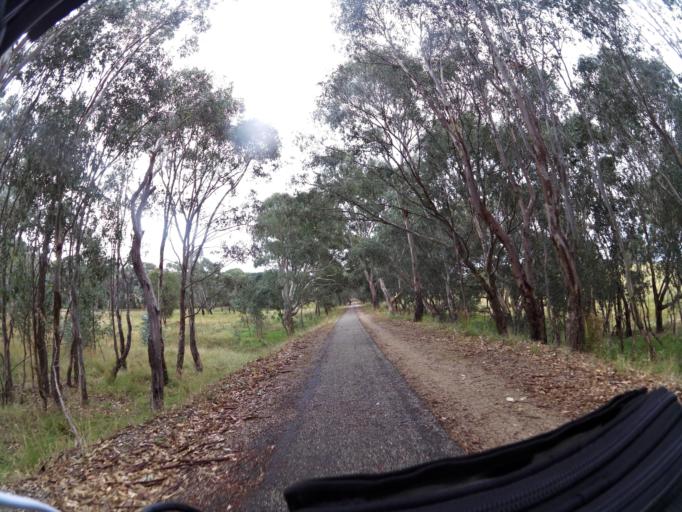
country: AU
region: New South Wales
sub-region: Albury Municipality
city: East Albury
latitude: -36.2233
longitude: 147.1143
